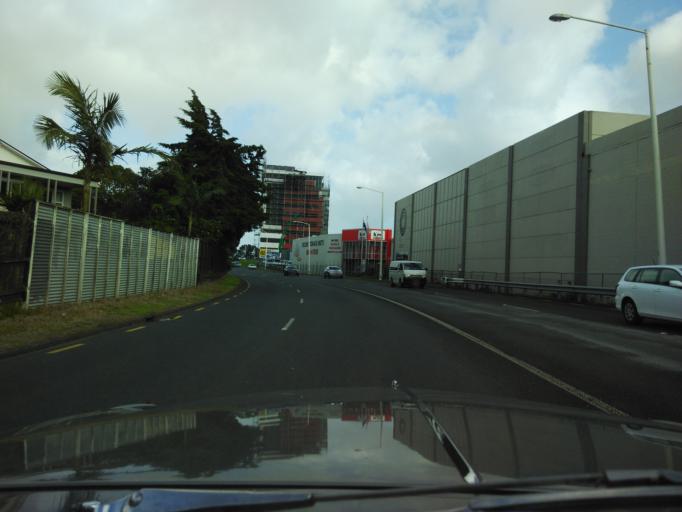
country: NZ
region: Auckland
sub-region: Auckland
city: Tamaki
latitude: -36.9008
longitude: 174.8136
